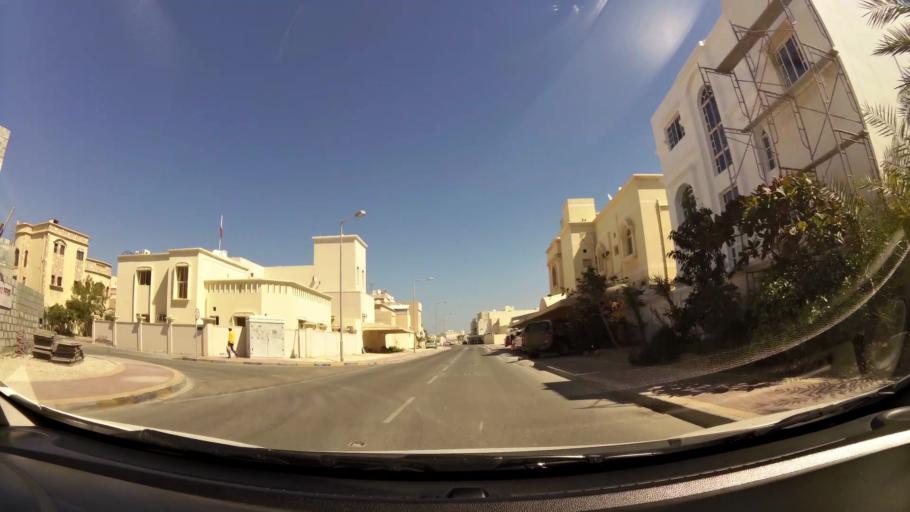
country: BH
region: Muharraq
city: Al Hadd
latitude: 26.2761
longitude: 50.6467
